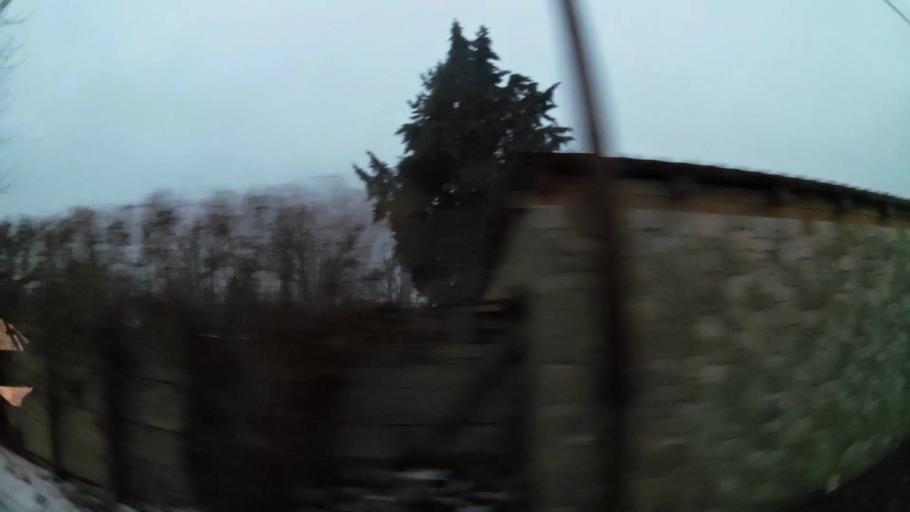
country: MK
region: Kisela Voda
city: Kisela Voda
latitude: 41.9729
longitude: 21.4913
